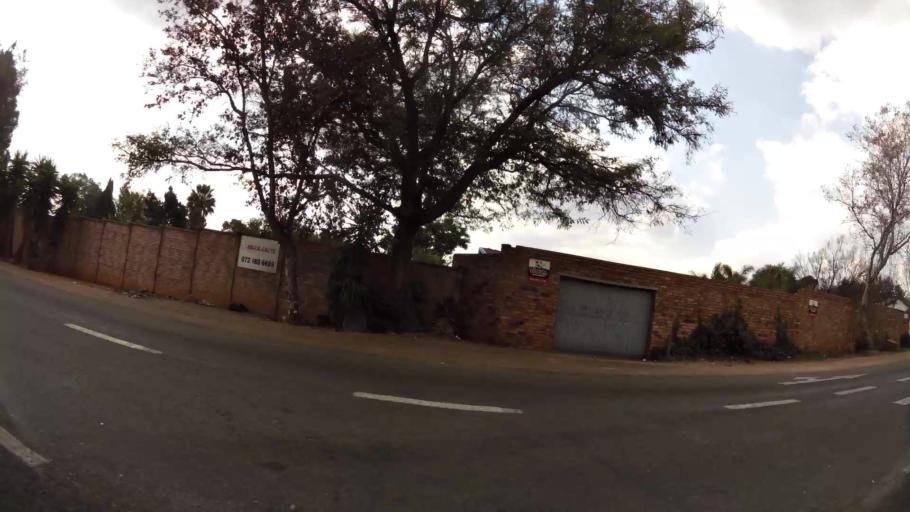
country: ZA
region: Gauteng
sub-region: City of Tshwane Metropolitan Municipality
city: Centurion
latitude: -25.8359
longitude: 28.2533
